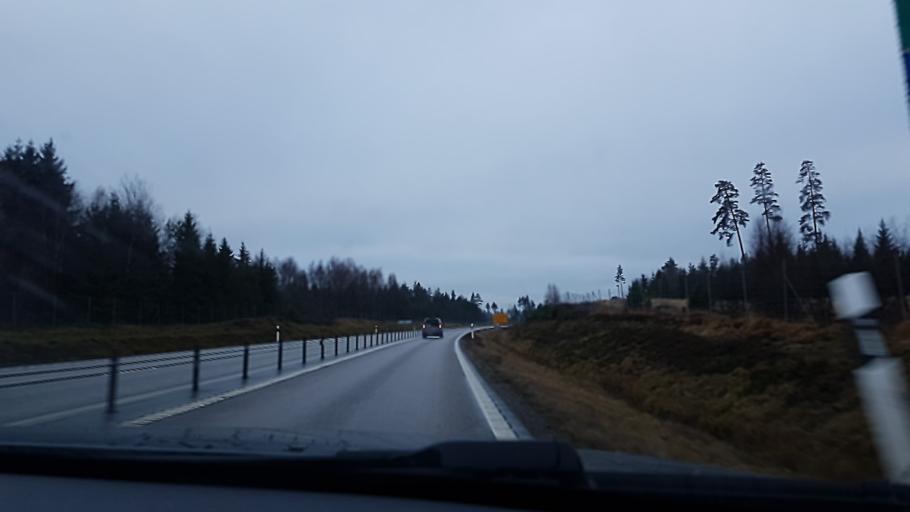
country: SE
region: Kronoberg
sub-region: Ljungby Kommun
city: Lagan
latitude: 56.9739
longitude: 14.0186
